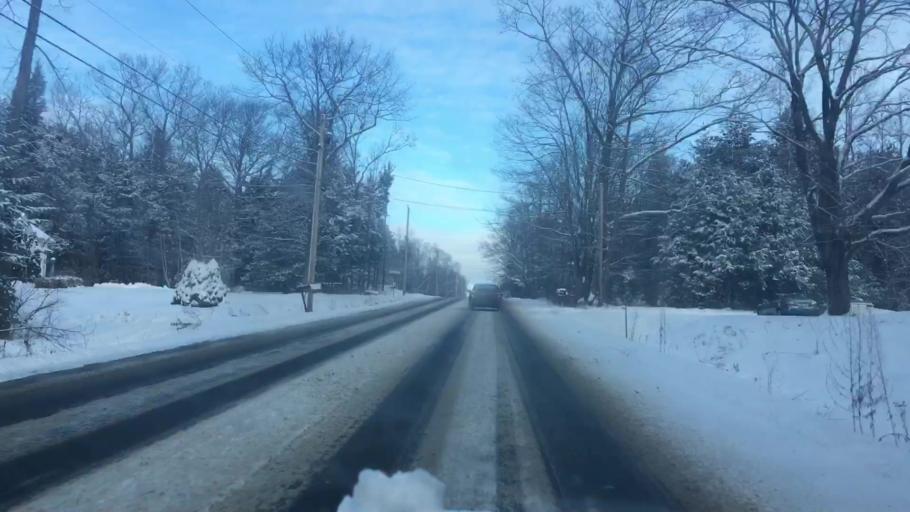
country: US
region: Maine
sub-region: Cumberland County
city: North Windham
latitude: 43.8055
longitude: -70.4406
